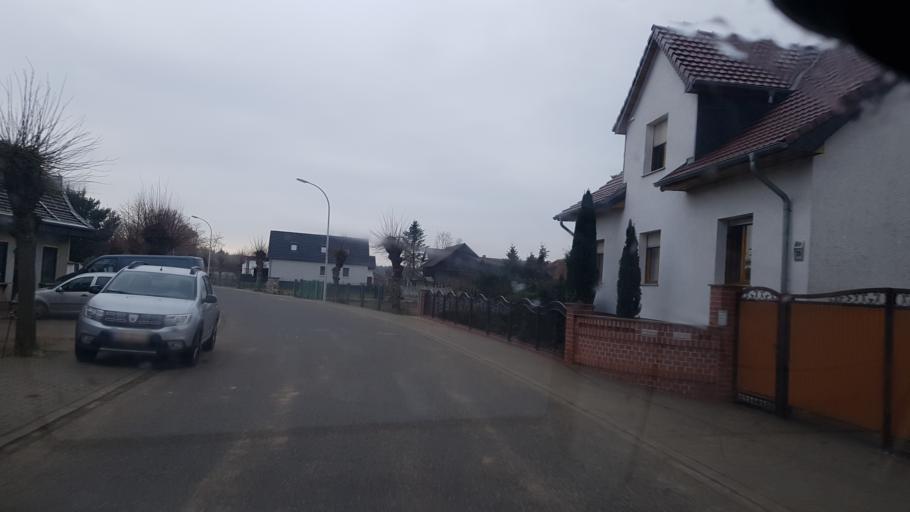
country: DE
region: Brandenburg
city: Cottbus
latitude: 51.7607
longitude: 14.4124
